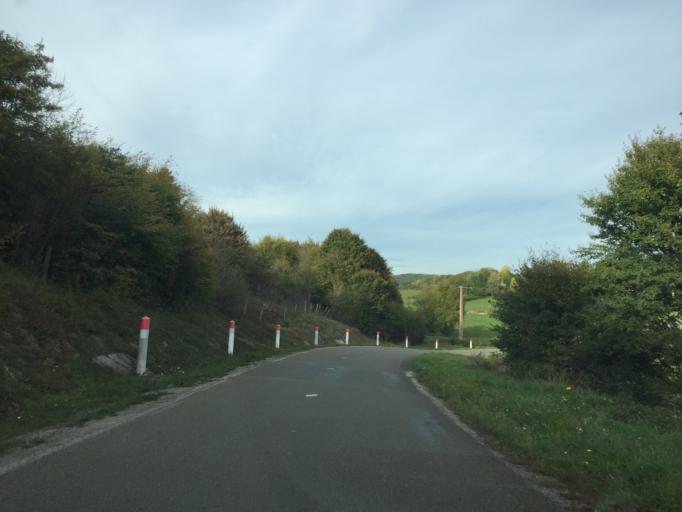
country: FR
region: Franche-Comte
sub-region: Departement du Jura
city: Orgelet
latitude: 46.5048
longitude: 5.5191
